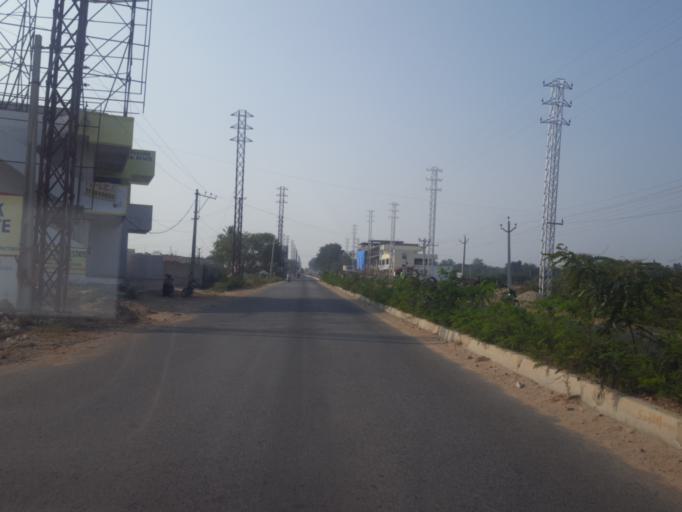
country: IN
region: Telangana
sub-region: Medak
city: Serilingampalle
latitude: 17.4036
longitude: 78.2880
